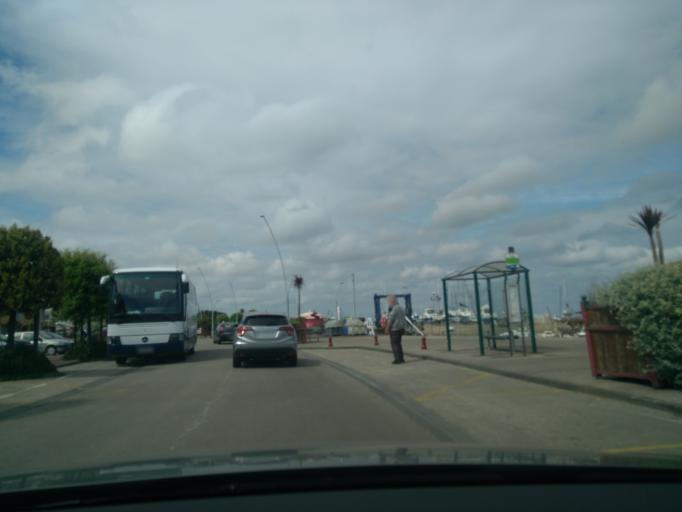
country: FR
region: Lower Normandy
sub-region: Departement de la Manche
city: Saint-Vaast-la-Hougue
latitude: 49.5888
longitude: -1.2661
